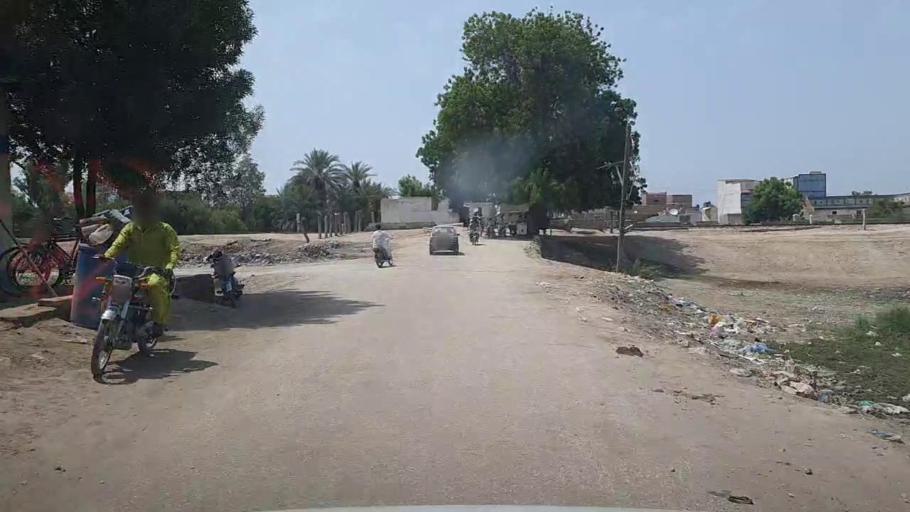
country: PK
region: Sindh
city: Pano Aqil
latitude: 27.8546
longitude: 69.1193
